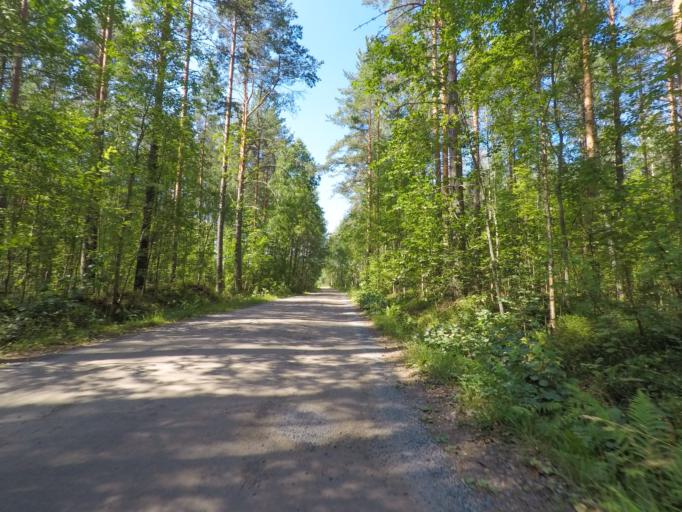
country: FI
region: Southern Savonia
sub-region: Mikkeli
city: Puumala
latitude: 61.4277
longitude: 28.0220
